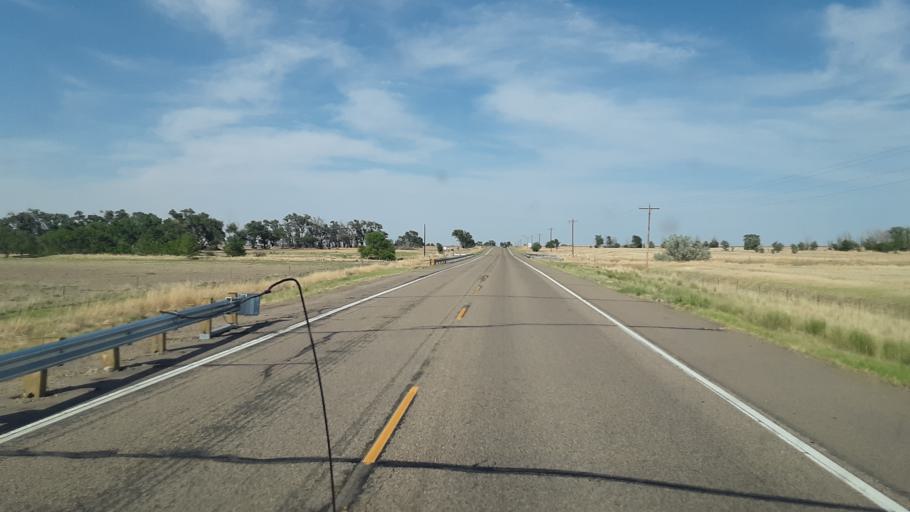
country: US
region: Colorado
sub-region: Bent County
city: Las Animas
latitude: 38.1092
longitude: -103.1083
